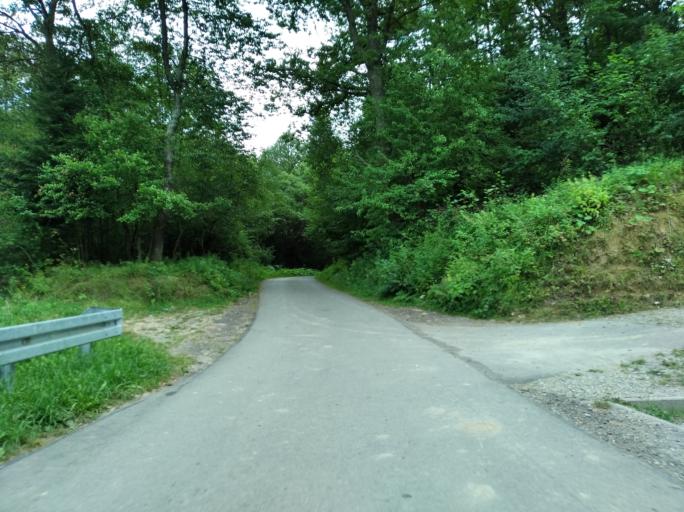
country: PL
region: Subcarpathian Voivodeship
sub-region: Powiat krosnienski
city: Wojaszowka
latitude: 49.7822
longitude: 21.7051
